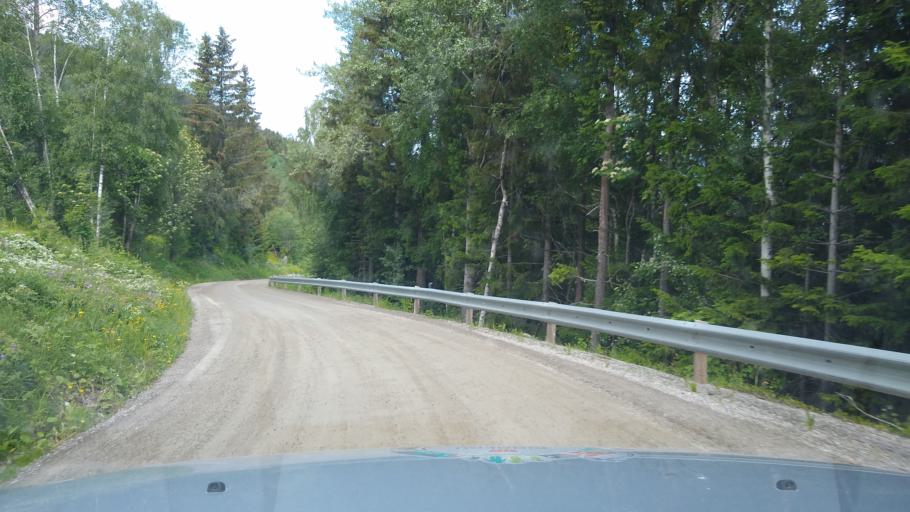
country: NO
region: Oppland
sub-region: Ringebu
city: Ringebu
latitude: 61.5103
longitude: 10.1363
